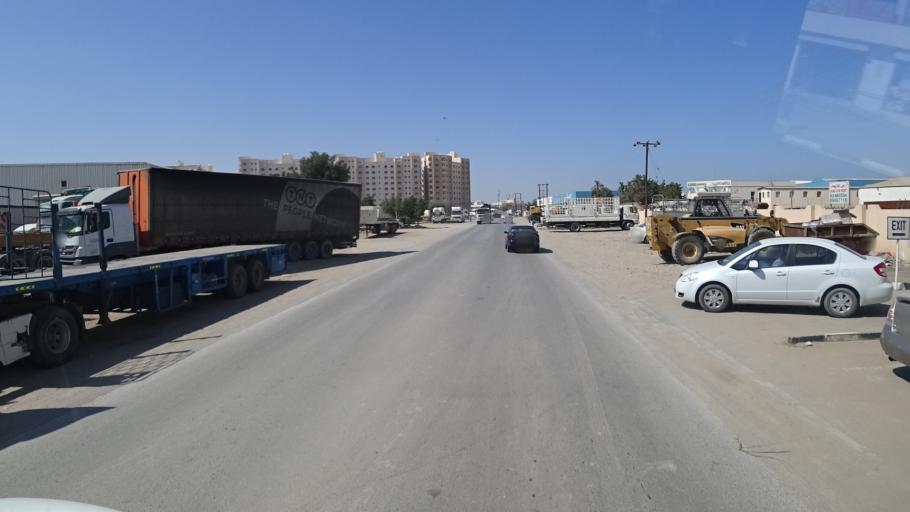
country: OM
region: Muhafazat Masqat
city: Bawshar
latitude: 23.5755
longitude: 58.3698
